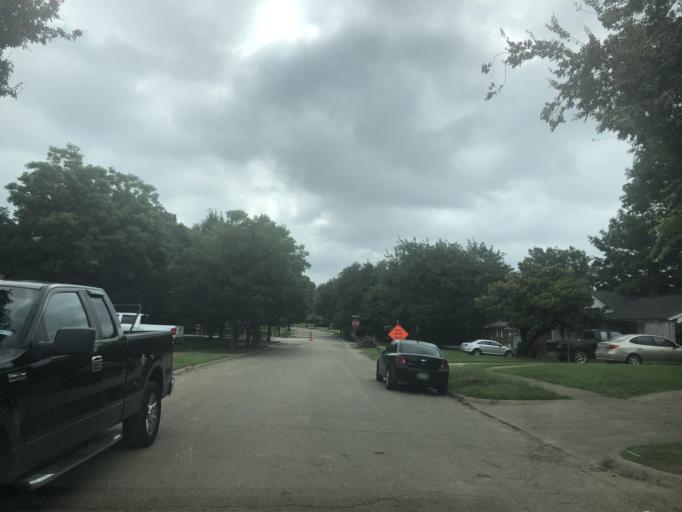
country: US
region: Texas
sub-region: Dallas County
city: University Park
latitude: 32.8627
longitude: -96.8513
